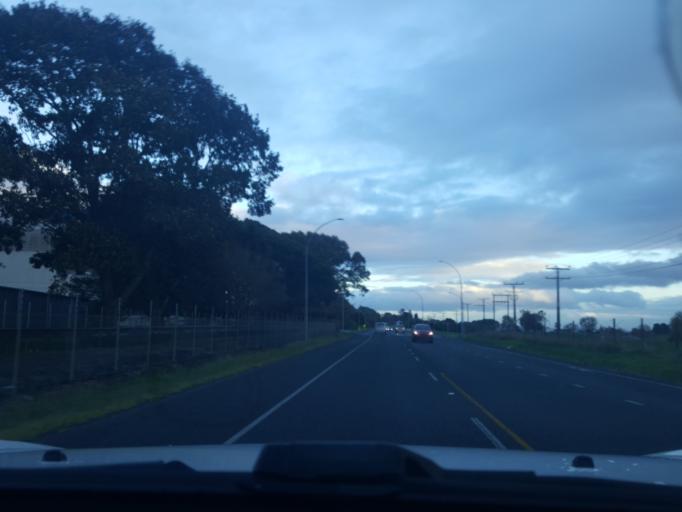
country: NZ
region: Waikato
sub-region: Waikato District
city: Ngaruawahia
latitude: -37.7168
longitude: 175.2126
